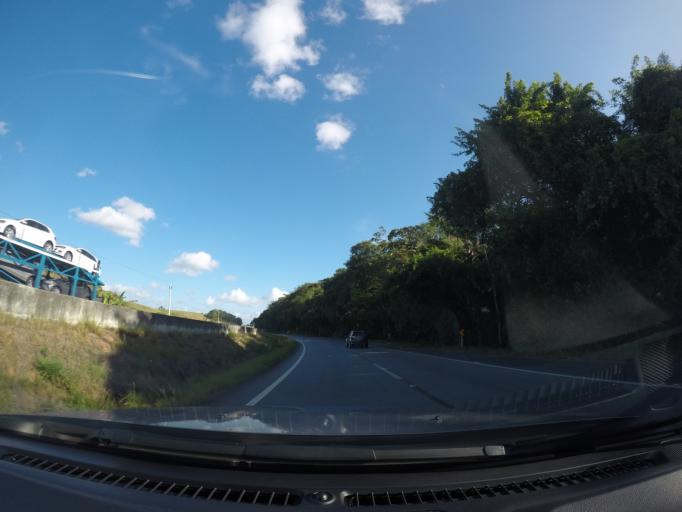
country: BR
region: Alagoas
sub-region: Messias
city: Messias
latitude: -9.3642
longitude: -35.8377
